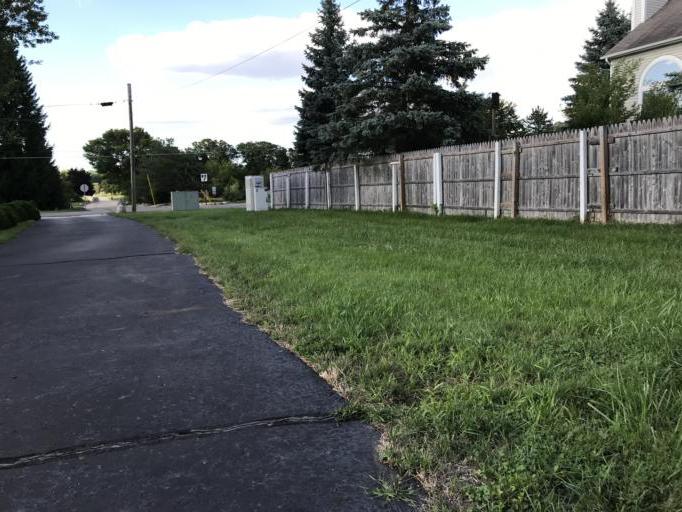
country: US
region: Michigan
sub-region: Oakland County
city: Farmington
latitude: 42.4700
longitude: -83.3470
